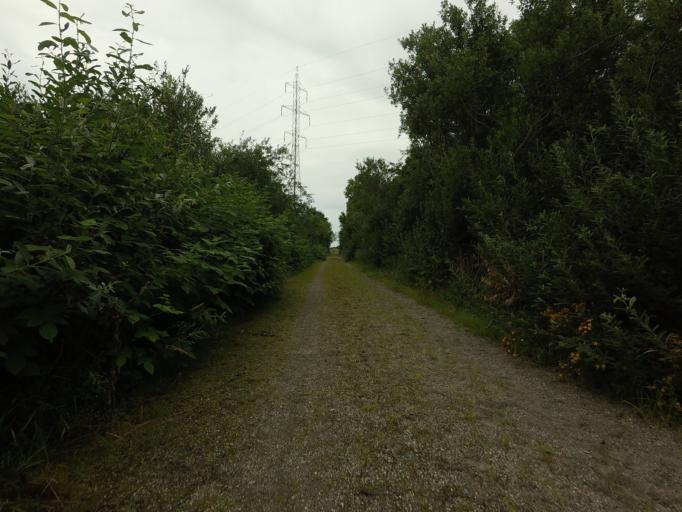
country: DK
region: North Denmark
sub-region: Alborg Kommune
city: Vadum
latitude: 57.1332
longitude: 9.8378
